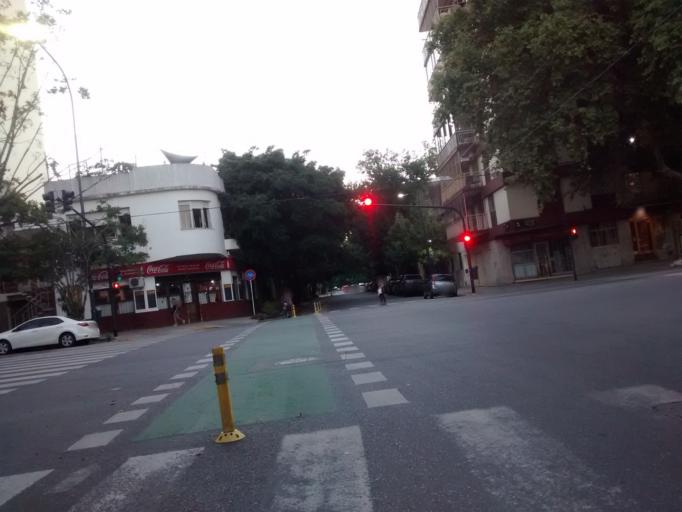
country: AR
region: Buenos Aires F.D.
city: Colegiales
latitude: -34.6028
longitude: -58.4494
